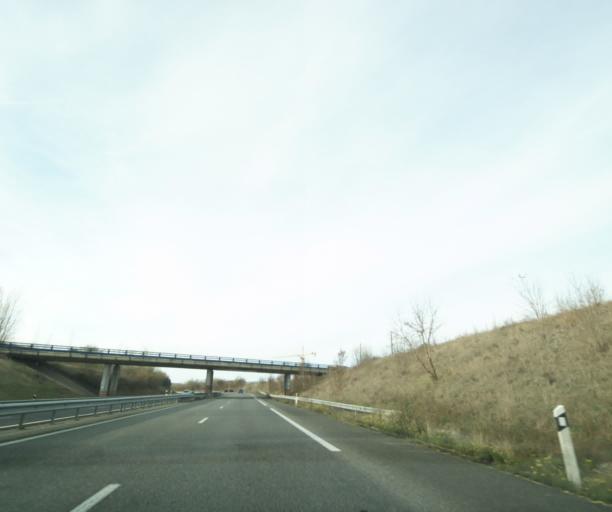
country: FR
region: Midi-Pyrenees
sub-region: Departement du Gers
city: Pujaudran
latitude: 43.6044
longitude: 1.0795
